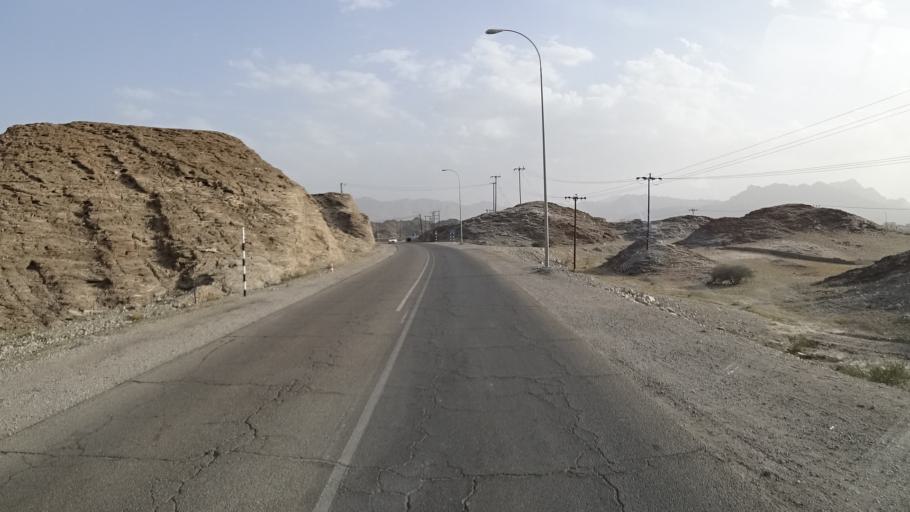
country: OM
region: Muhafazat Masqat
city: Bawshar
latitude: 23.3831
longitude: 58.5126
